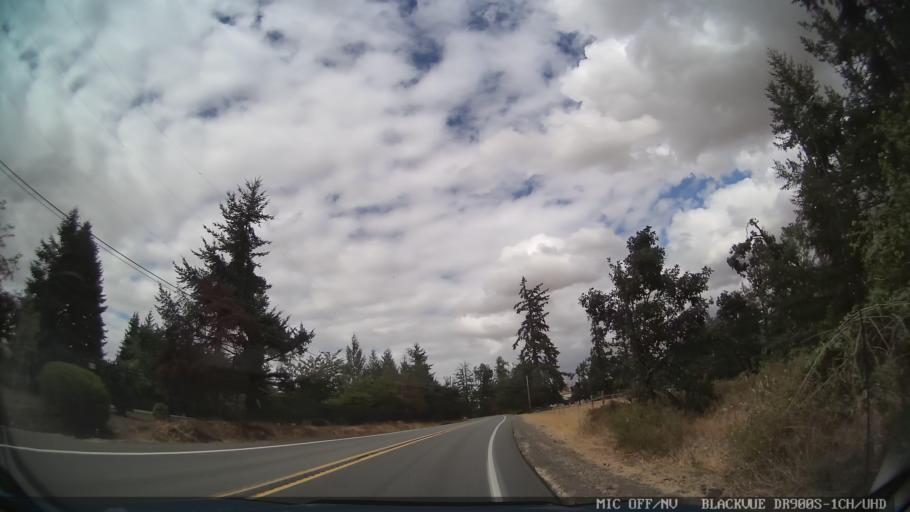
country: US
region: Oregon
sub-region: Marion County
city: Sublimity
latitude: 44.8496
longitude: -122.7941
